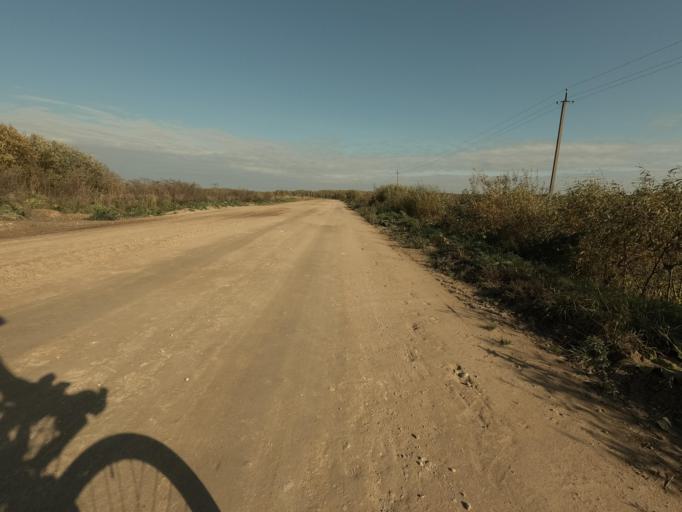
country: RU
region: Novgorod
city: Batetskiy
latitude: 58.8183
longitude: 30.7006
